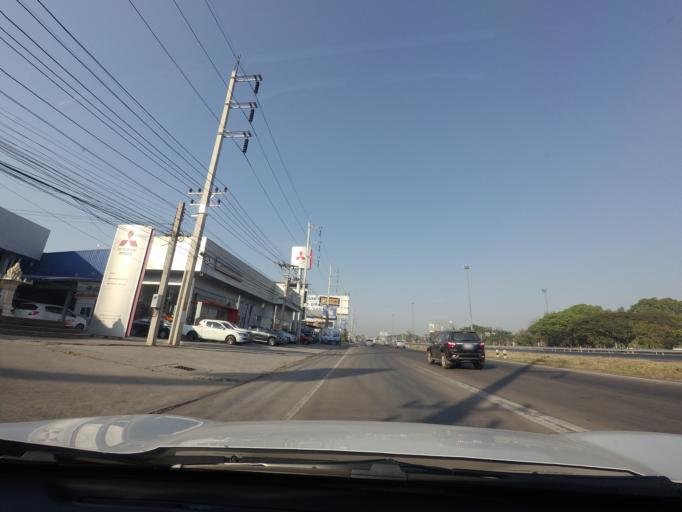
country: TH
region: Nakhon Ratchasima
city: Pak Chong
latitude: 14.6616
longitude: 101.4024
